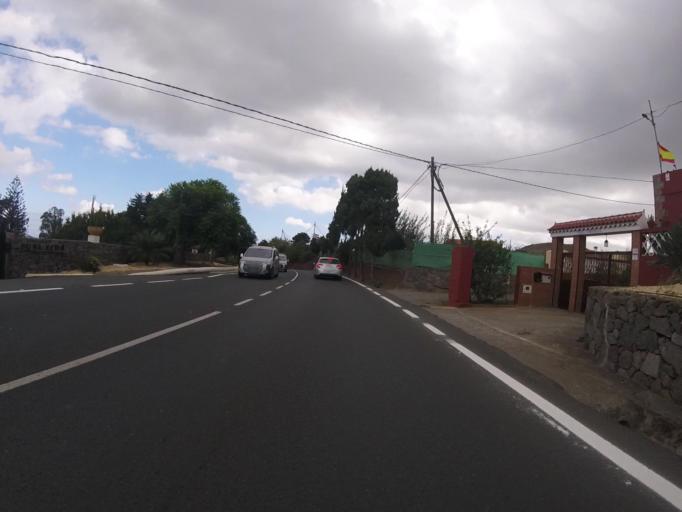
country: ES
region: Canary Islands
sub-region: Provincia de Las Palmas
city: Vega de San Mateo
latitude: 28.0160
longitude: -15.5247
